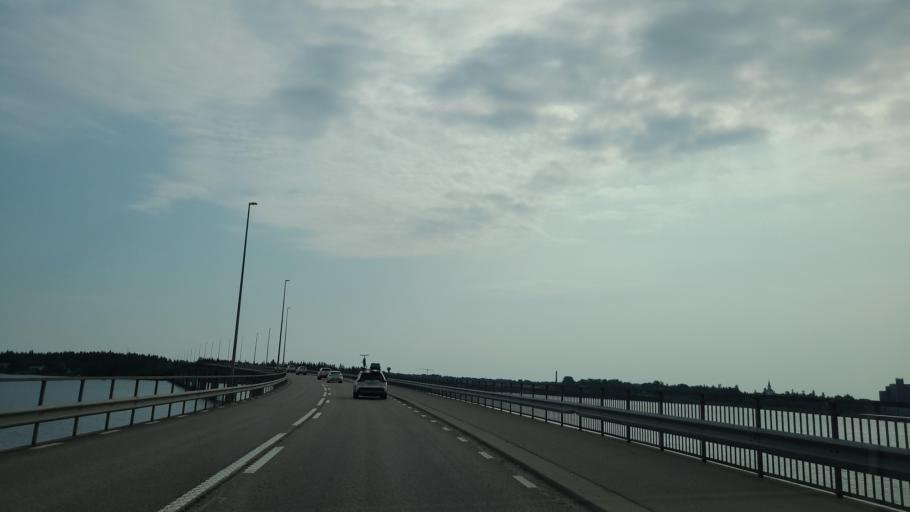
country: SE
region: Vaesterbotten
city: Obbola
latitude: 63.7101
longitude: 20.3289
